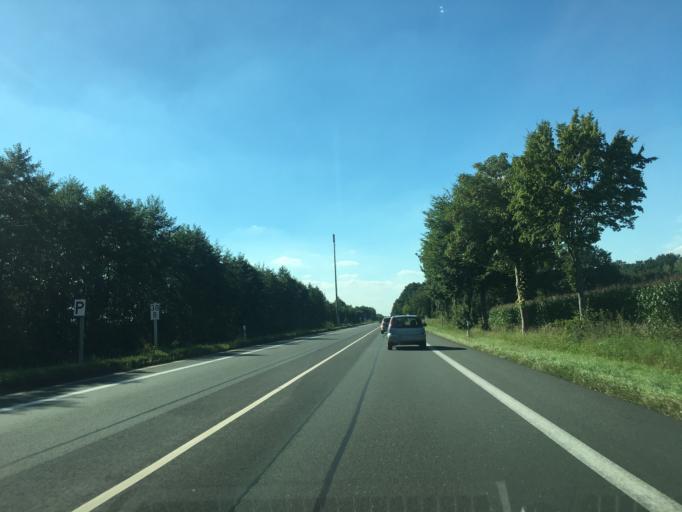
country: DE
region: North Rhine-Westphalia
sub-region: Regierungsbezirk Munster
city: Beelen
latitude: 51.9136
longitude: 8.1643
